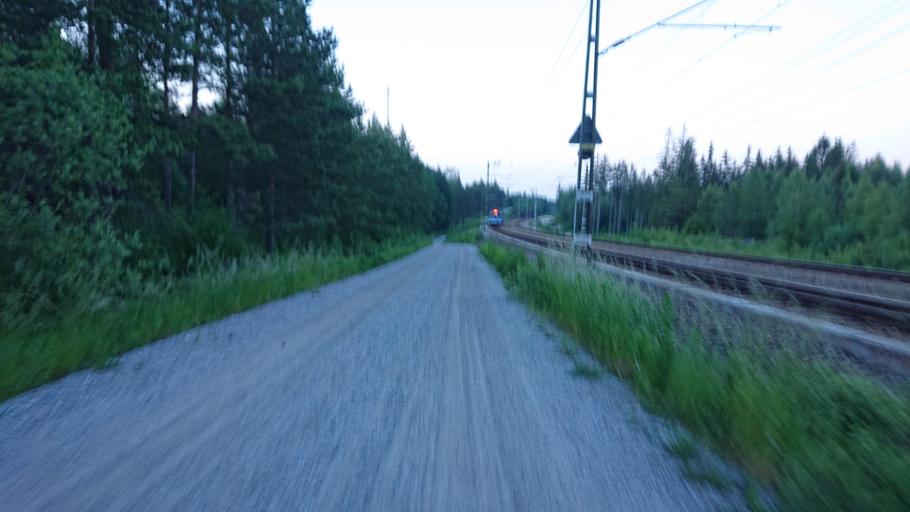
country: SE
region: Stockholm
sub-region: Osterakers Kommun
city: Akersberga
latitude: 59.4676
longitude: 18.1972
